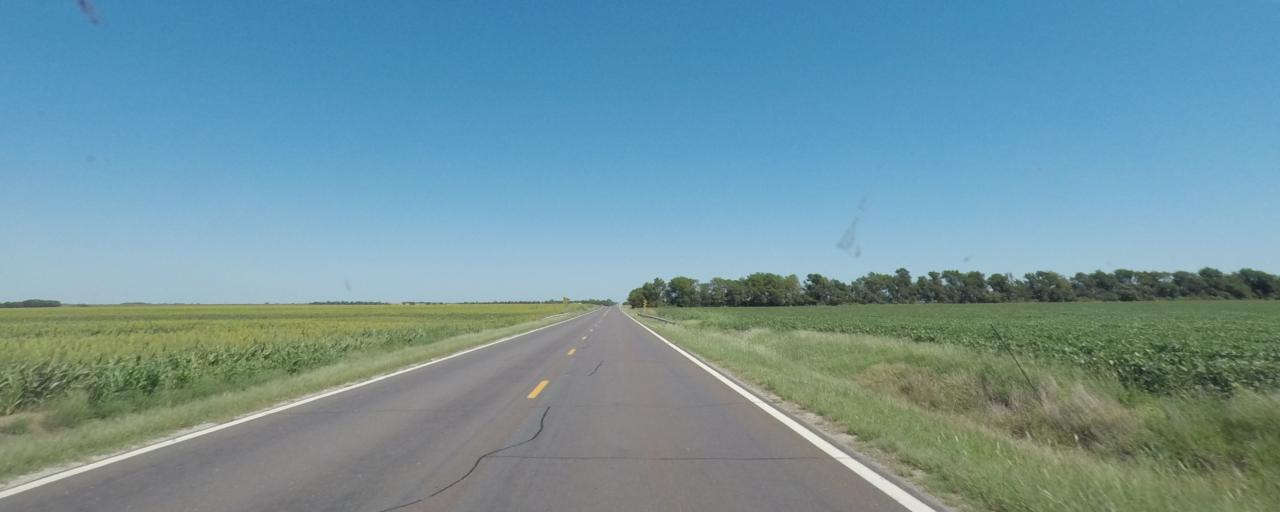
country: US
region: Kansas
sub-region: Sumner County
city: Wellington
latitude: 37.1784
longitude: -97.4020
